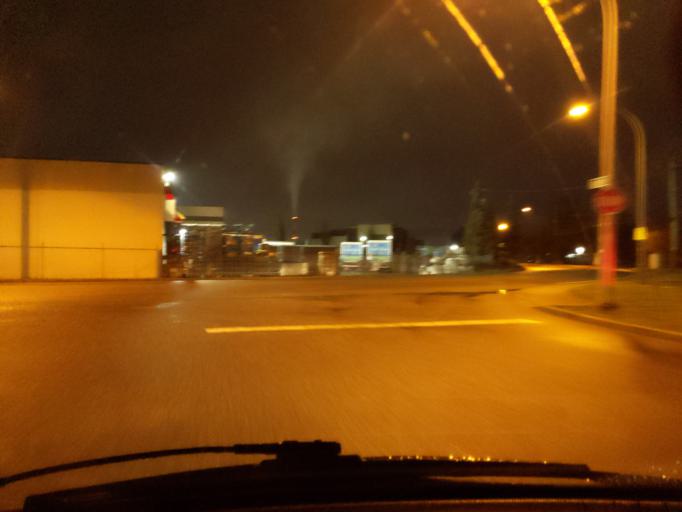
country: CA
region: British Columbia
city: Walnut Grove
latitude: 49.1778
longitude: -122.6735
